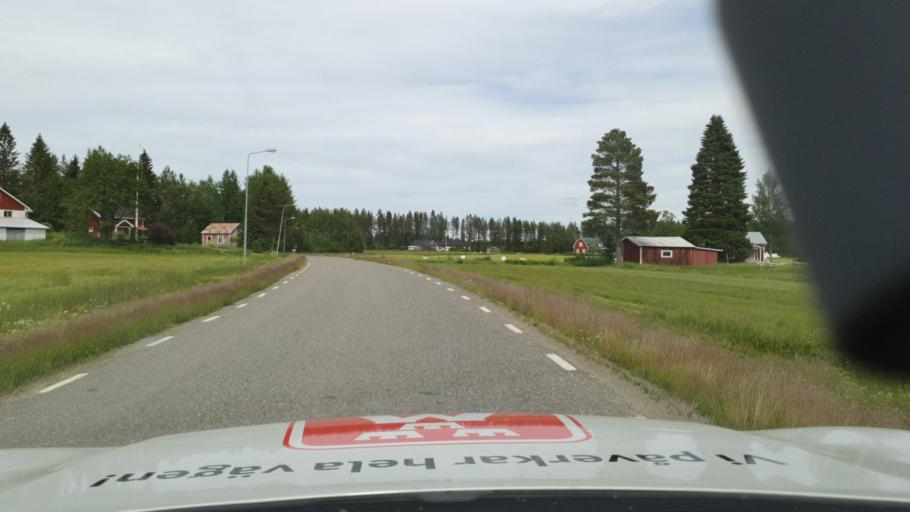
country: SE
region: Vaesterbotten
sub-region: Skelleftea Kommun
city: Viken
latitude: 64.4979
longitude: 20.9095
